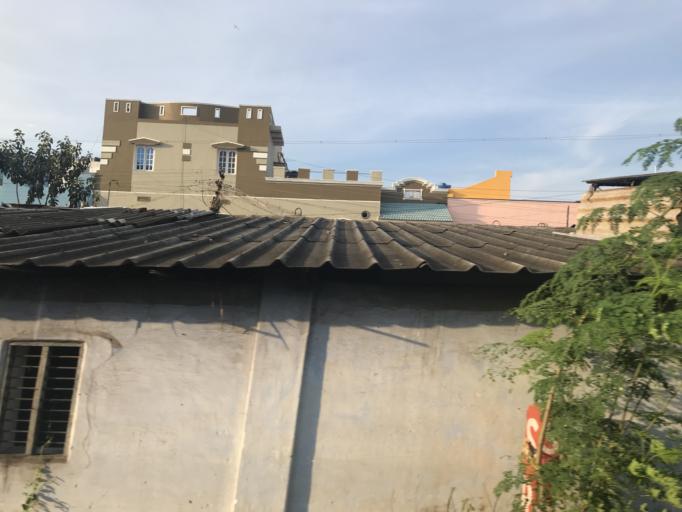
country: IN
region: Tamil Nadu
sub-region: Coimbatore
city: Coimbatore
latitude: 11.0315
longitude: 76.9635
